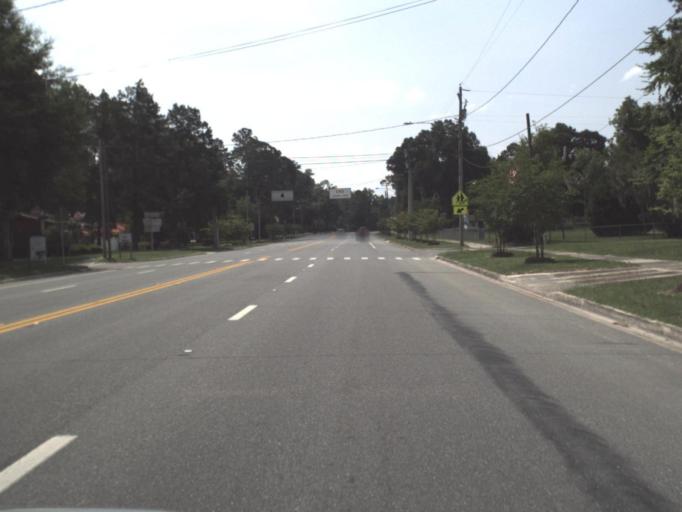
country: US
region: Georgia
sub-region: Echols County
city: Statenville
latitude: 30.6024
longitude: -83.0994
